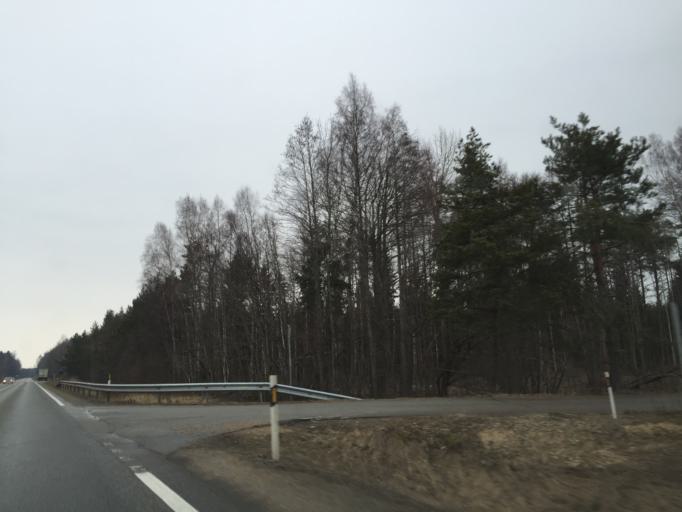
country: LV
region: Salacgrivas
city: Salacgriva
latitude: 57.6140
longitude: 24.3951
